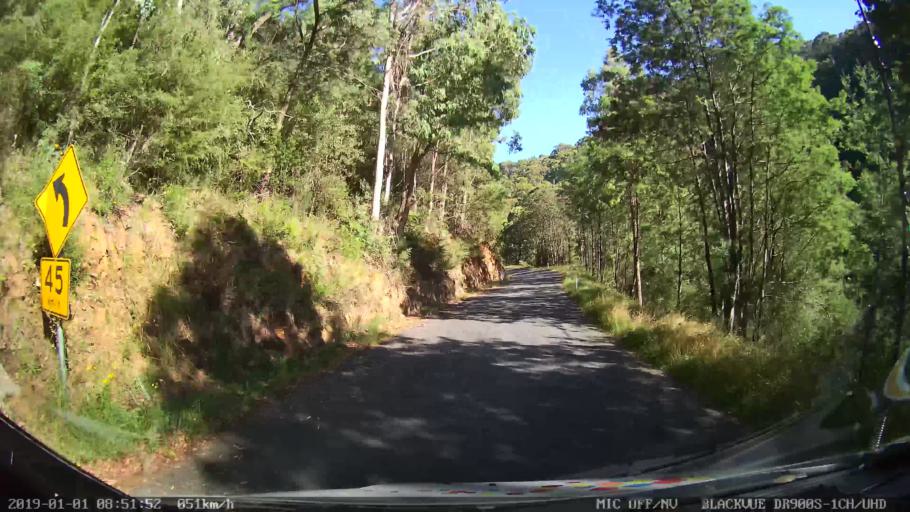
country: AU
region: New South Wales
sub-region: Snowy River
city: Jindabyne
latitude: -36.2687
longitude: 148.2012
